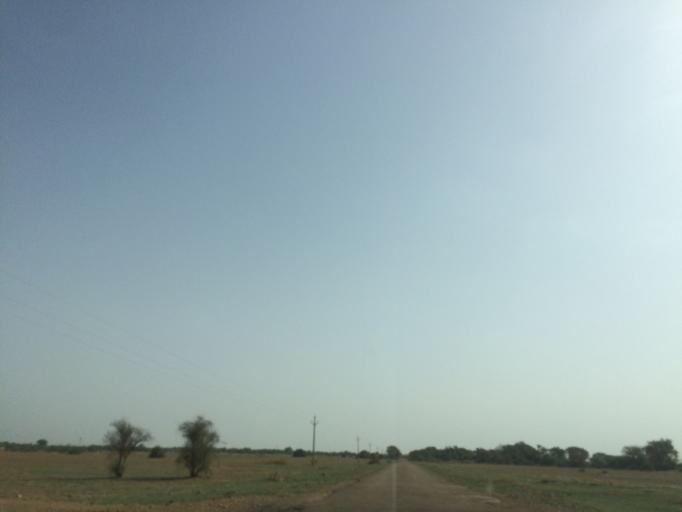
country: IN
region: Rajasthan
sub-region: Jaisalmer
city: Jaisalmer
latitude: 26.8668
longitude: 70.7715
